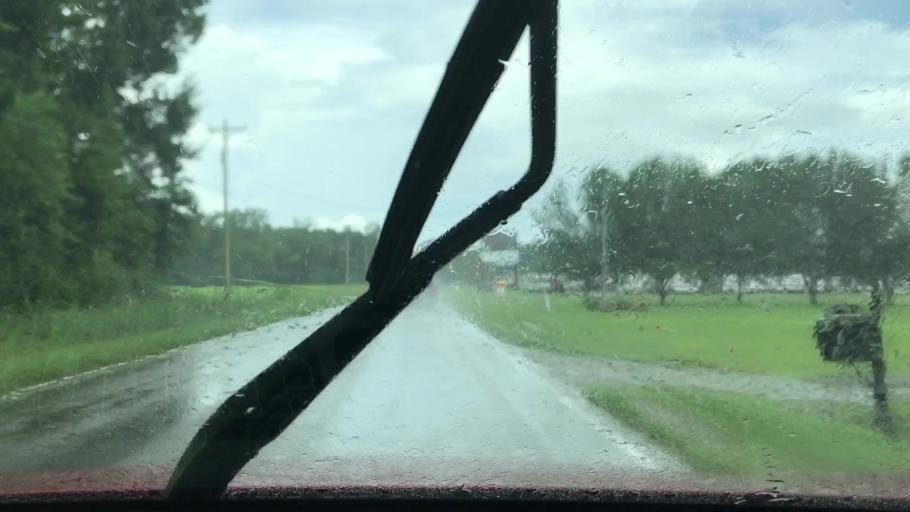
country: US
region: South Carolina
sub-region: Horry County
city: Red Hill
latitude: 33.8620
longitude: -78.9934
